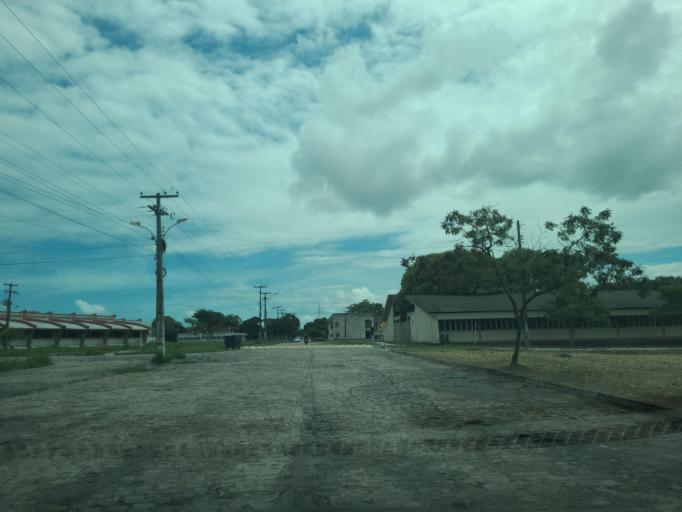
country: BR
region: Alagoas
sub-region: Satuba
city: Satuba
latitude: -9.5544
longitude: -35.7726
